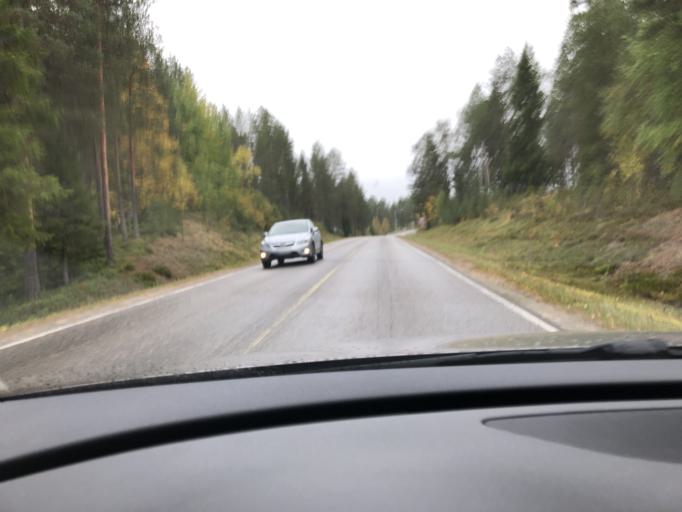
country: FI
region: Lapland
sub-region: Itae-Lappi
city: Posio
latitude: 66.1168
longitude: 28.1824
